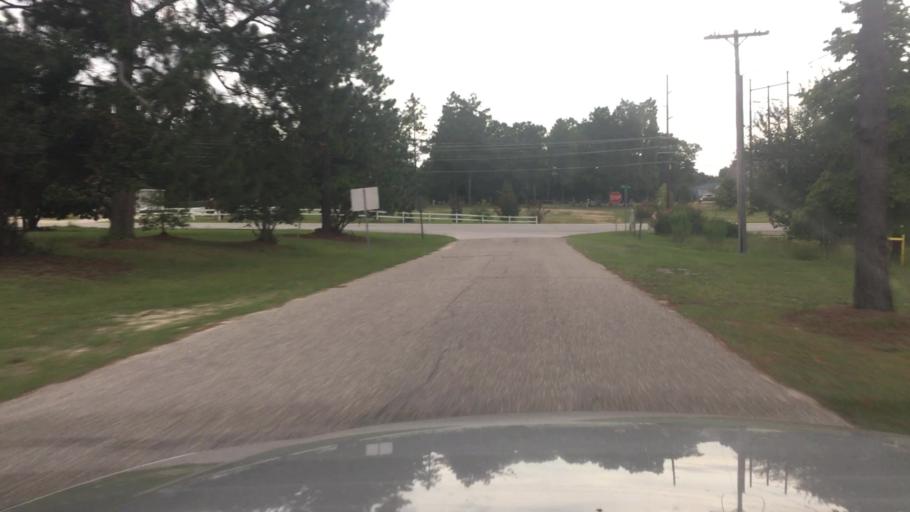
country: US
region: North Carolina
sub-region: Hoke County
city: Rockfish
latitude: 34.9821
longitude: -79.0341
